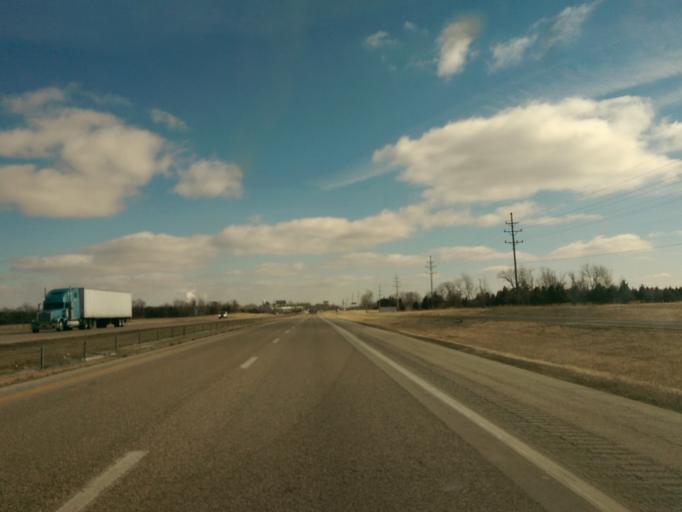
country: US
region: Missouri
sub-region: Montgomery County
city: Montgomery City
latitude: 38.8837
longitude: -91.4011
